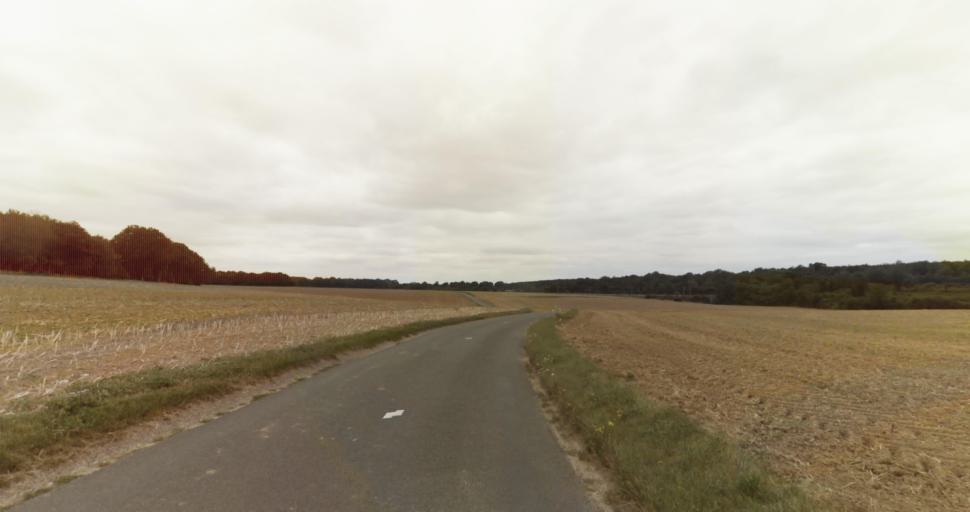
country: FR
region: Haute-Normandie
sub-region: Departement de l'Eure
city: Evreux
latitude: 48.9877
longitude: 1.2304
